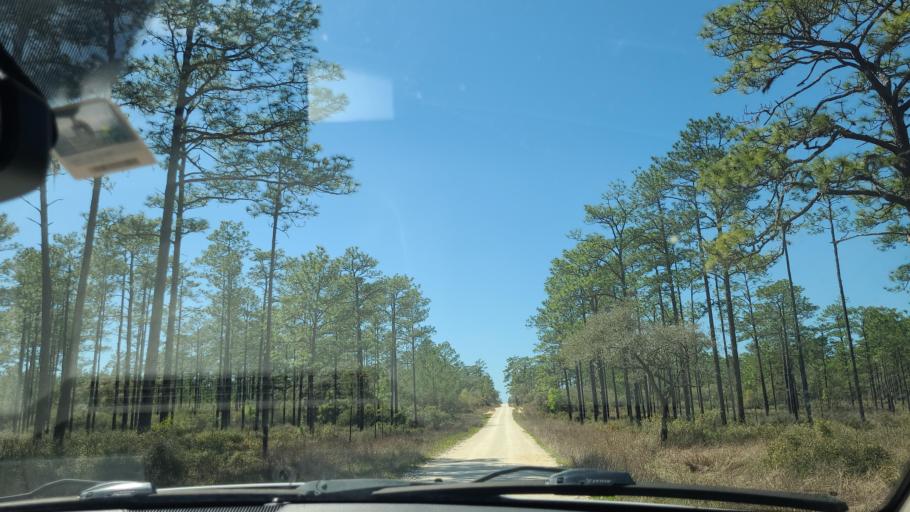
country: US
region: Florida
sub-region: Putnam County
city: Interlachen
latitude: 29.4288
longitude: -81.8098
